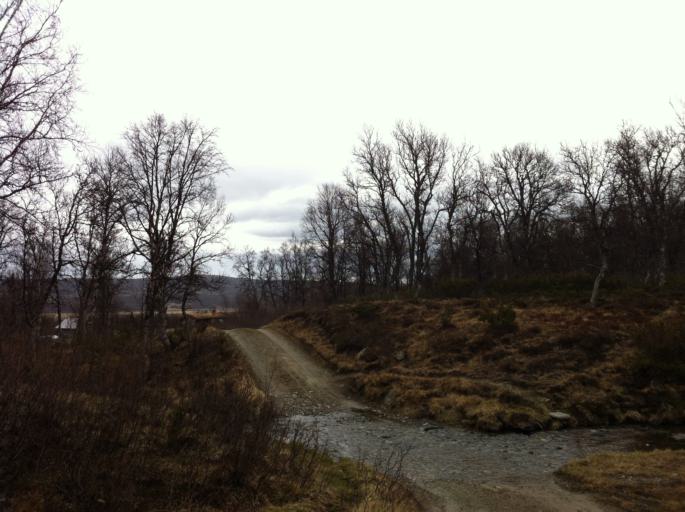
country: NO
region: Sor-Trondelag
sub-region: Tydal
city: Aas
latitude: 62.7064
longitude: 12.4903
